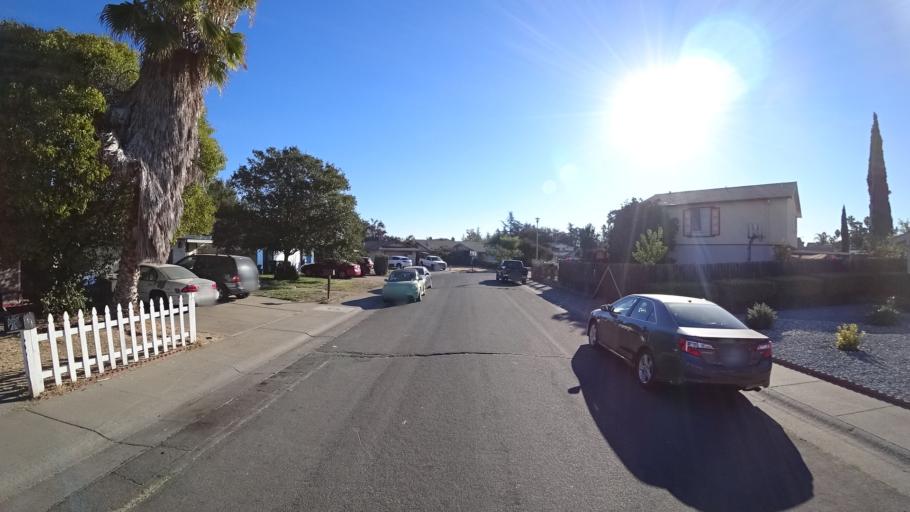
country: US
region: California
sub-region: Sacramento County
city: Parkway
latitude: 38.4928
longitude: -121.4622
